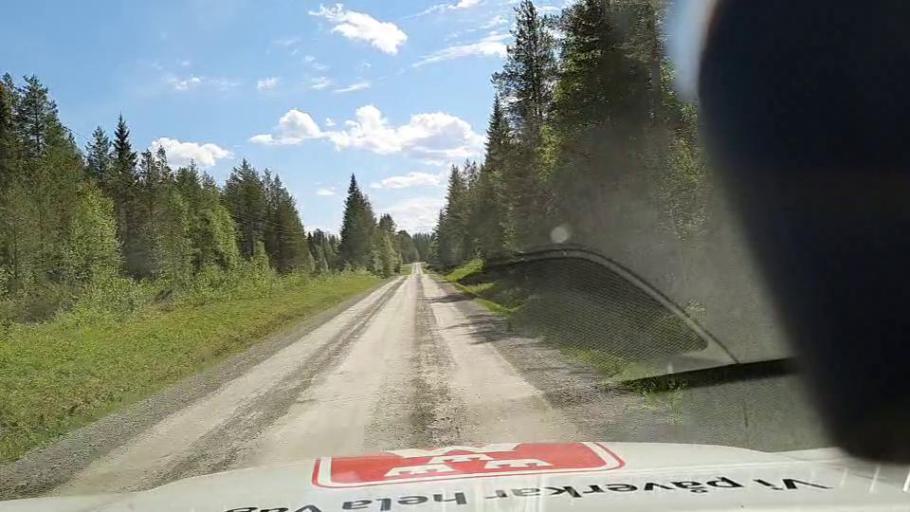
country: SE
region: Jaemtland
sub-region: Stroemsunds Kommun
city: Stroemsund
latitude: 64.4592
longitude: 15.5912
